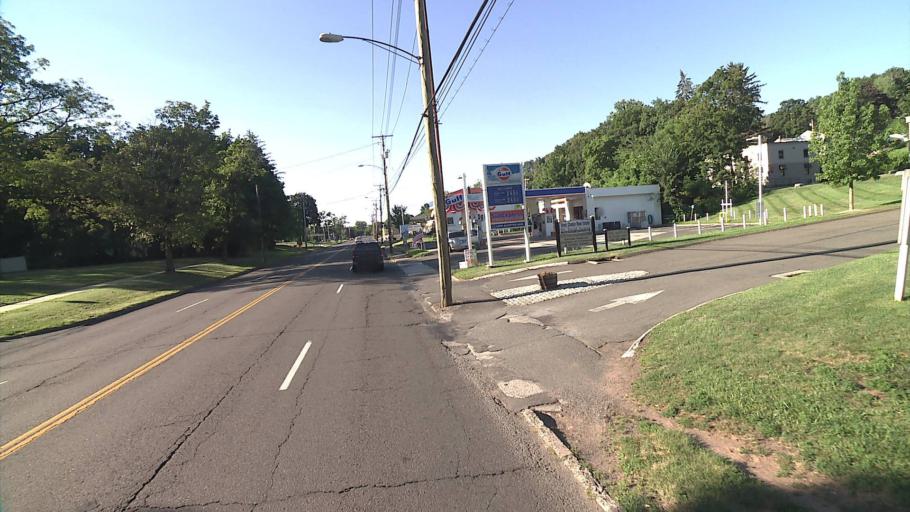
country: US
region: Connecticut
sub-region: New Haven County
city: Hamden
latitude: 41.4072
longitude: -72.8997
